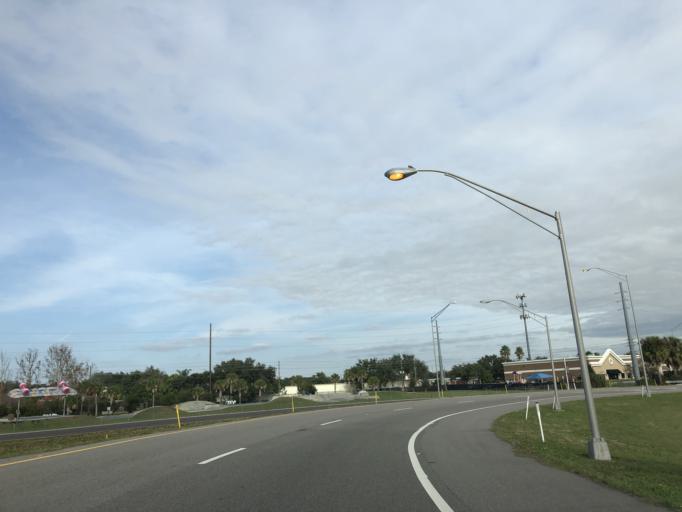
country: US
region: Florida
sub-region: Orange County
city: Hunters Creek
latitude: 28.3749
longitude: -81.4072
